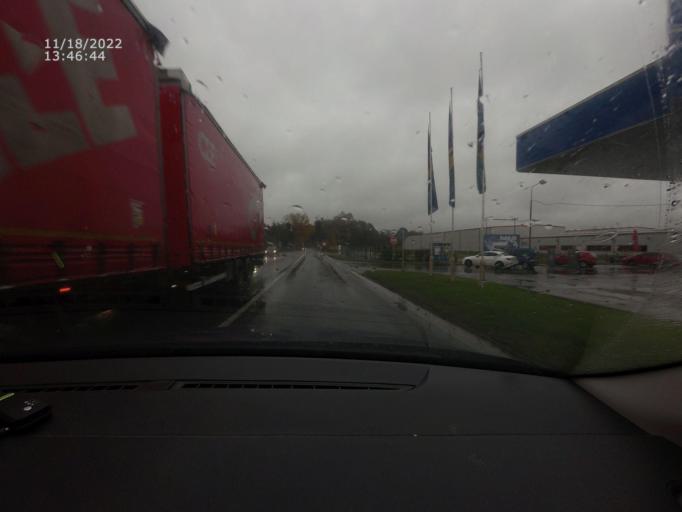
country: CZ
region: Jihocesky
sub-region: Okres Strakonice
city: Blatna
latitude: 49.4246
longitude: 13.8659
